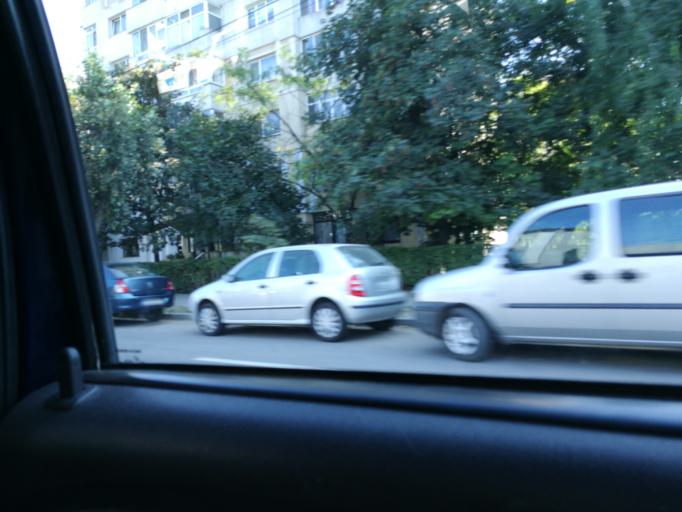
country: RO
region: Iasi
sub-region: Comuna Miroslava
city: Miroslava
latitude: 47.1730
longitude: 27.5540
